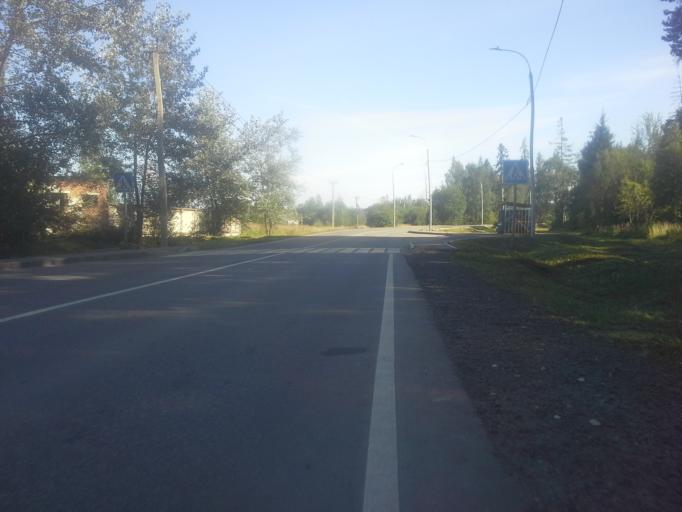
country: RU
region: Moskovskaya
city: Selyatino
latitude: 55.4183
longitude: 37.0091
